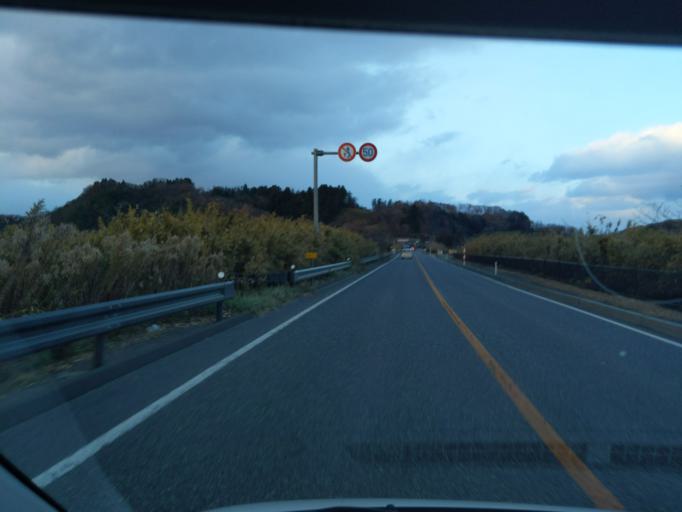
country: JP
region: Iwate
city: Ichinoseki
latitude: 38.7774
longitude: 141.0437
